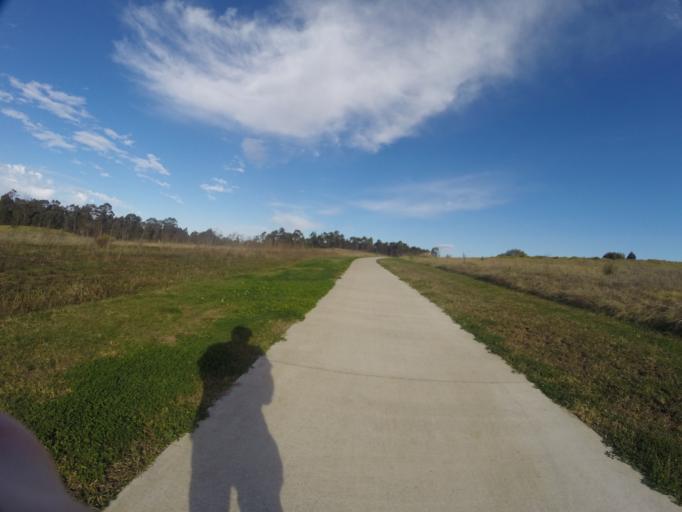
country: AU
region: New South Wales
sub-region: Fairfield
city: Horsley Park
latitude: -33.8553
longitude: 150.8725
